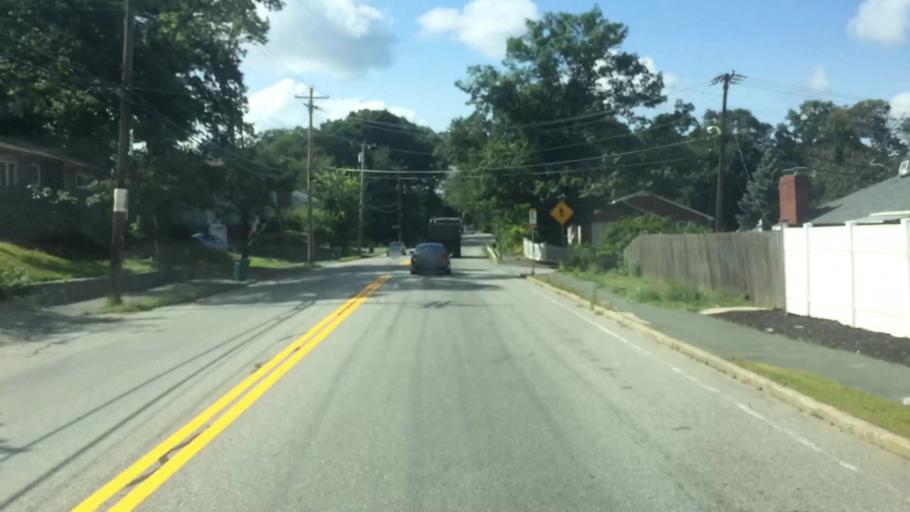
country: US
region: Massachusetts
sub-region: Essex County
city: South Peabody
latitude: 42.4999
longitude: -70.9755
